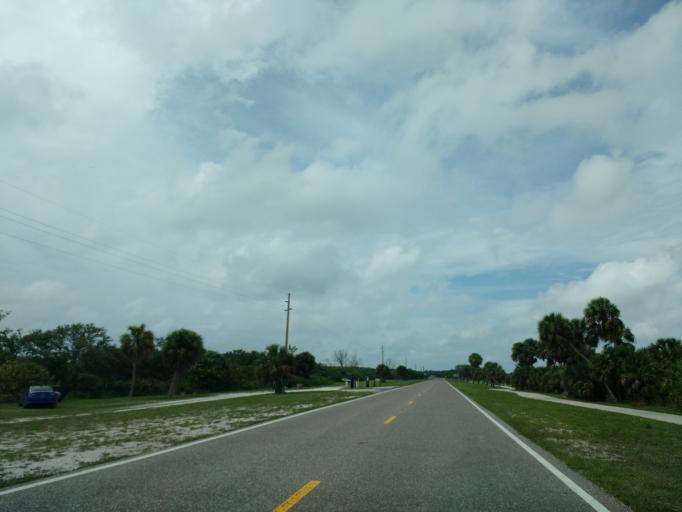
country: US
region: Florida
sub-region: Pinellas County
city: Tierra Verde
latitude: 27.6382
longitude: -82.7169
